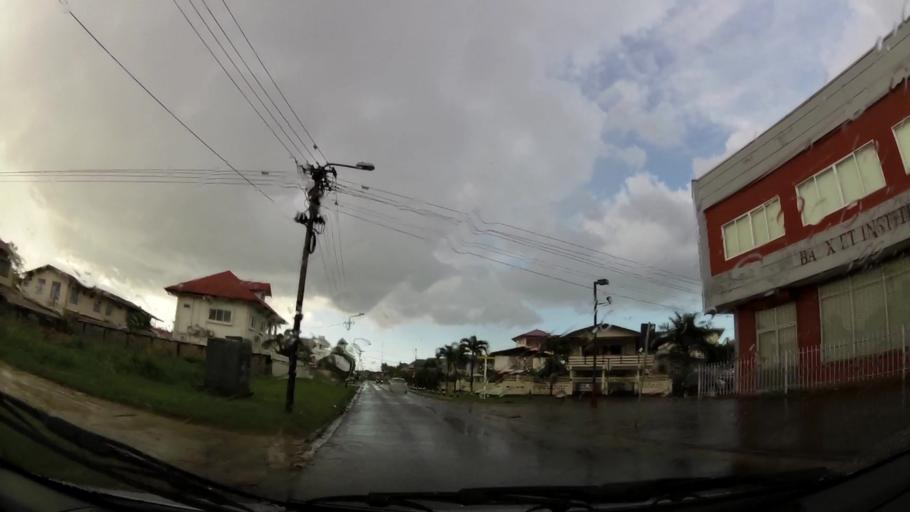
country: SR
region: Paramaribo
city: Paramaribo
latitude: 5.8233
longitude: -55.1847
